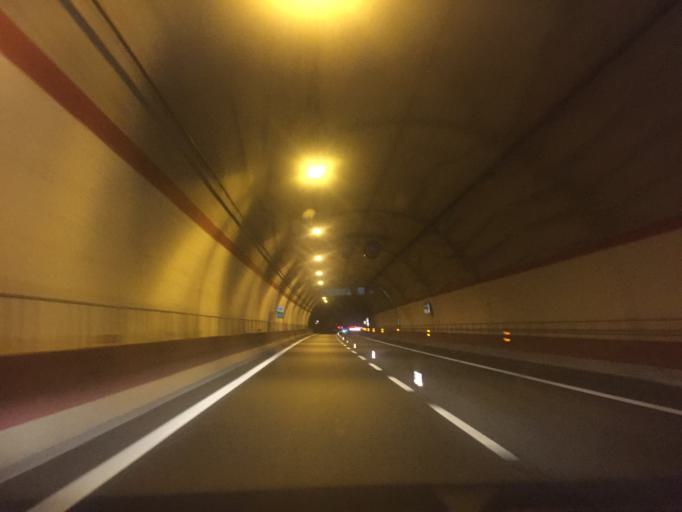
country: IT
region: Sicily
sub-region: Provincia di Siracusa
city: Carlentini
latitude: 37.3074
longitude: 15.0585
